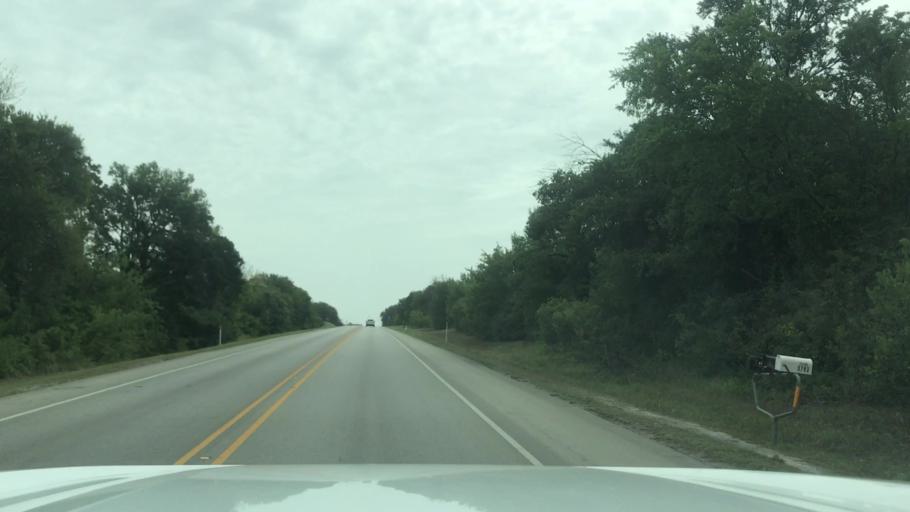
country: US
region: Texas
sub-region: Erath County
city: Dublin
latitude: 32.0984
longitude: -98.3927
